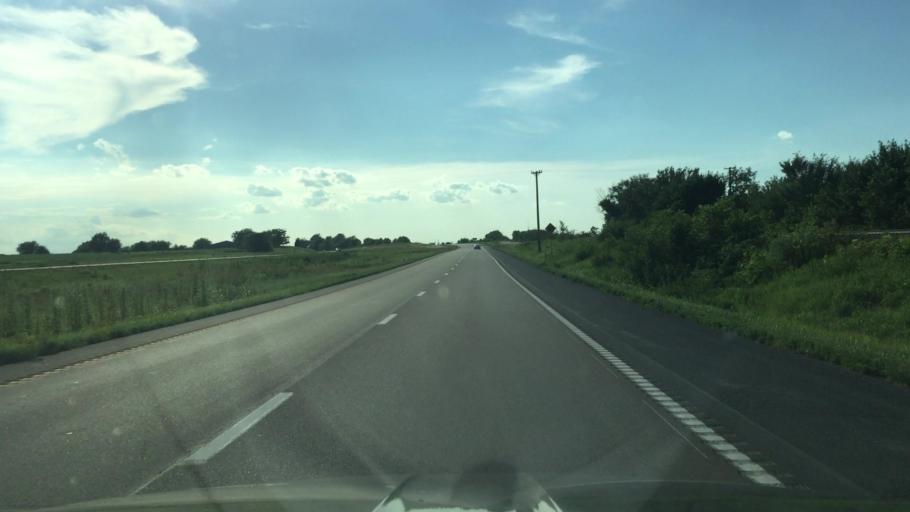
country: US
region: Missouri
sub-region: Pettis County
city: La Monte
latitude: 38.7597
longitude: -93.3712
